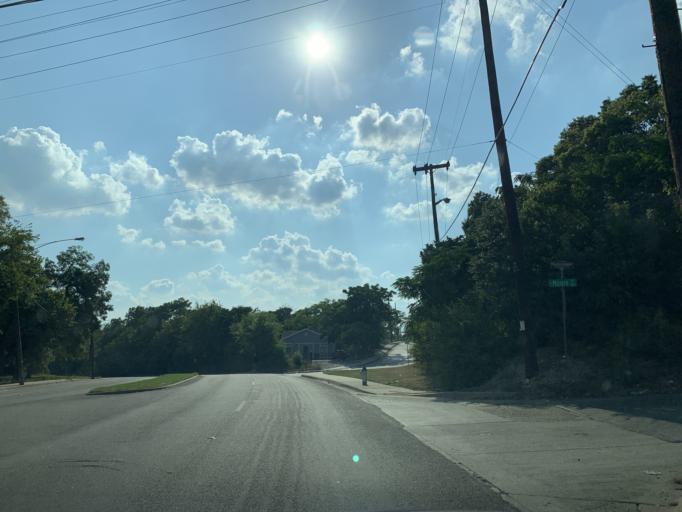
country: US
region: Texas
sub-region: Dallas County
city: Dallas
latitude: 32.7483
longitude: -96.8038
